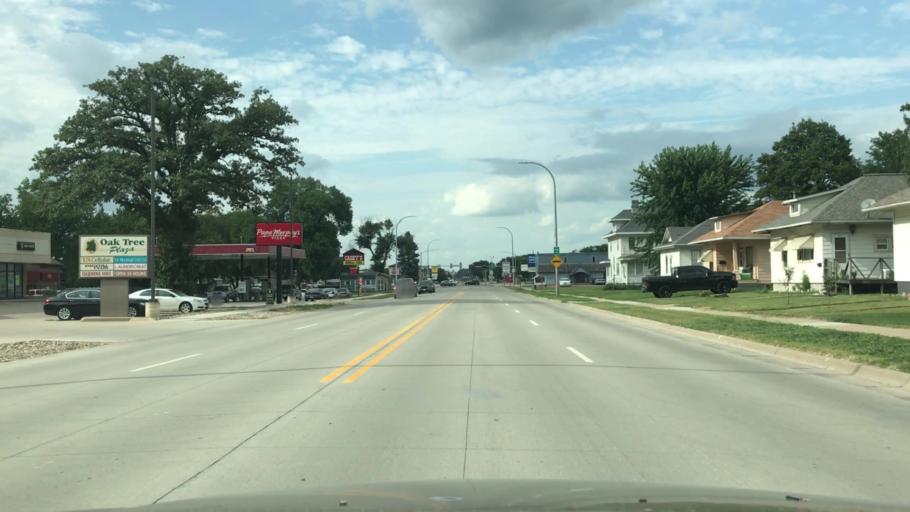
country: US
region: Iowa
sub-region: Plymouth County
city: Le Mars
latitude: 42.7907
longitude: -96.1738
